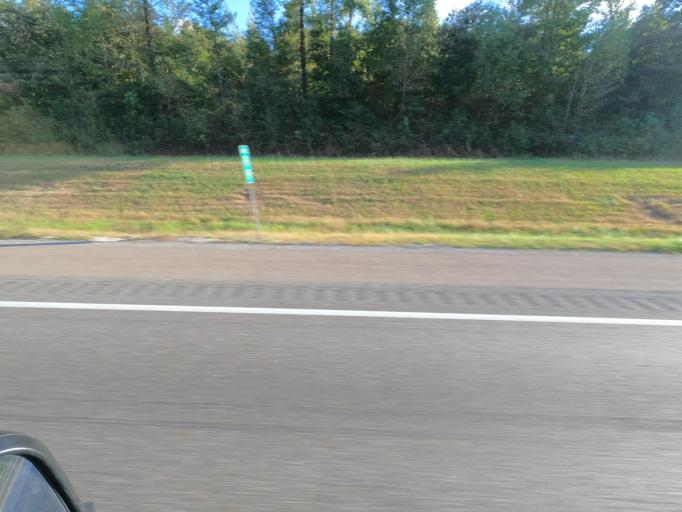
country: US
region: Tennessee
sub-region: Henderson County
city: Lexington
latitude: 35.7492
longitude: -88.5437
